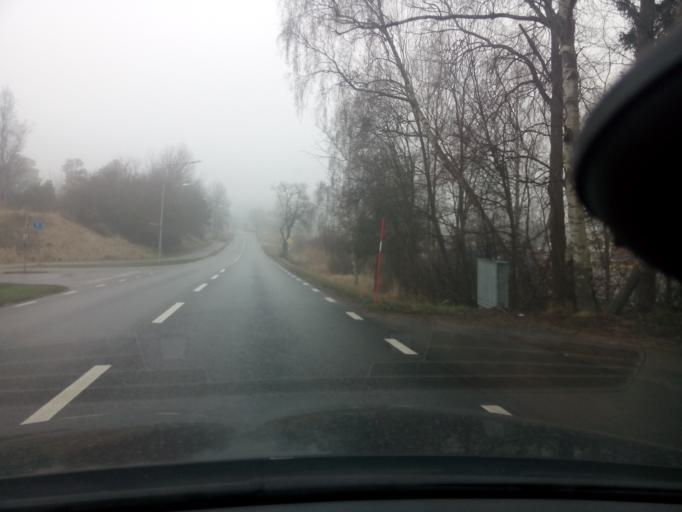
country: SE
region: Soedermanland
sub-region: Nykopings Kommun
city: Nykoping
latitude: 58.7694
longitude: 17.0298
